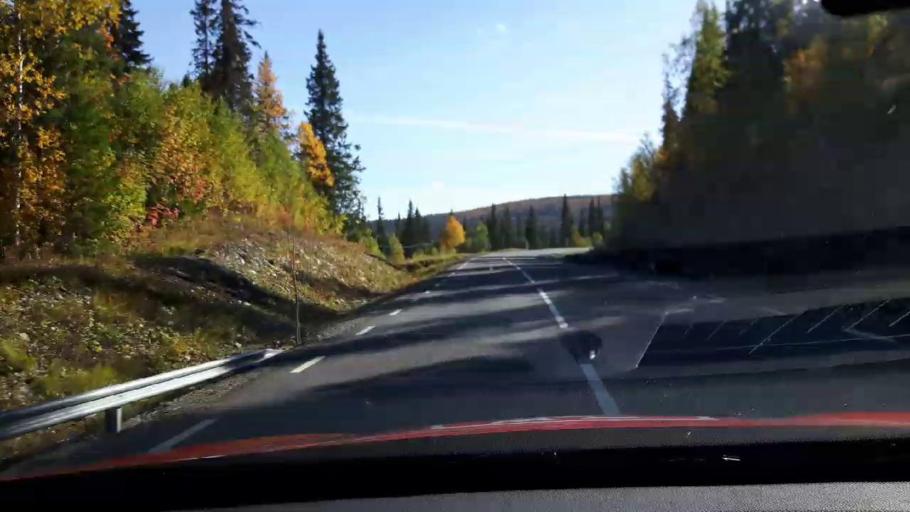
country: NO
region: Nord-Trondelag
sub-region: Royrvik
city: Royrvik
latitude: 64.8573
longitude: 14.1802
